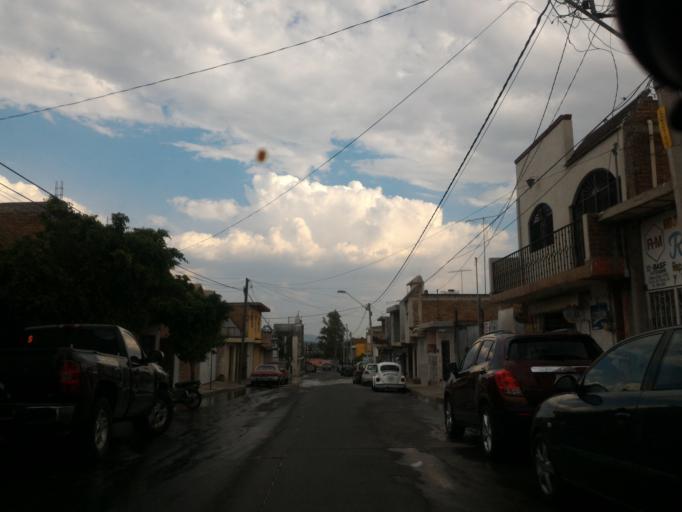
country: MX
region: Guanajuato
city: San Francisco del Rincon
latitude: 21.0405
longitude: -101.8563
